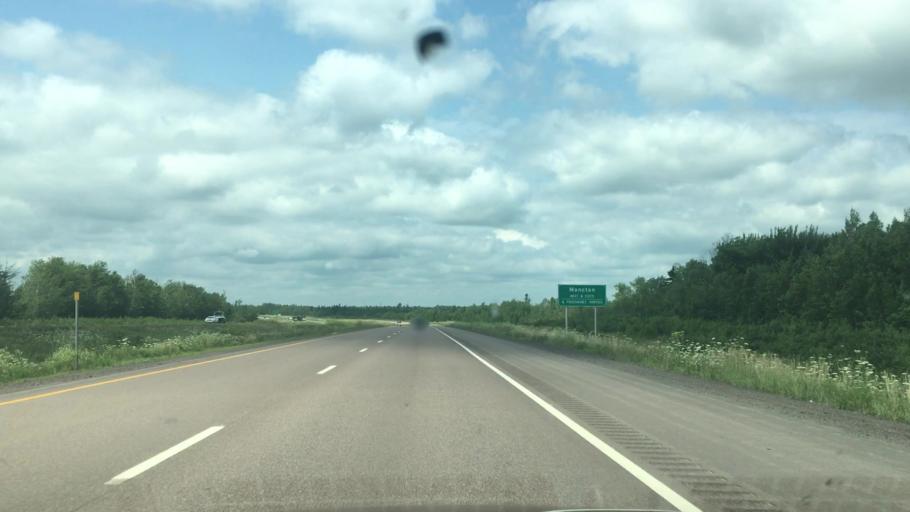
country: CA
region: New Brunswick
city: Dieppe
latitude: 46.1223
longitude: -64.6326
